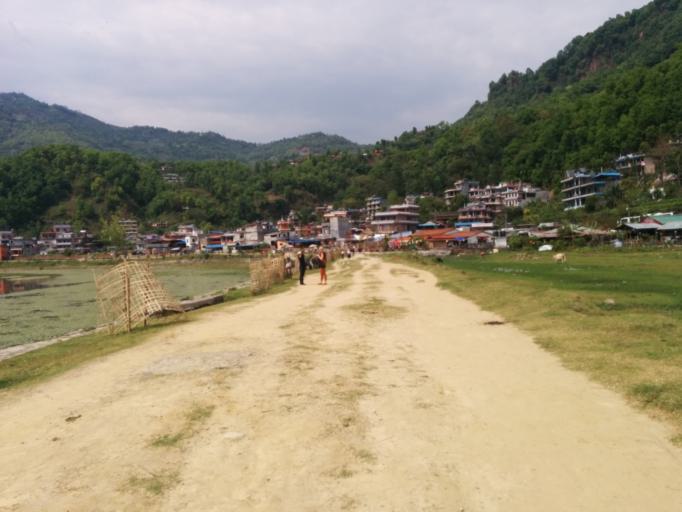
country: NP
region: Western Region
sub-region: Gandaki Zone
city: Pokhara
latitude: 28.2181
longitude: 83.9576
